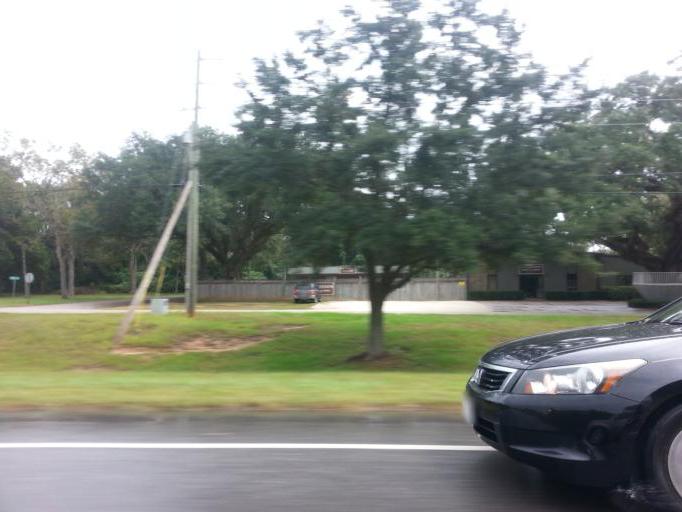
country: US
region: Alabama
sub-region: Baldwin County
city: Daphne
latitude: 30.5760
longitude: -87.8975
